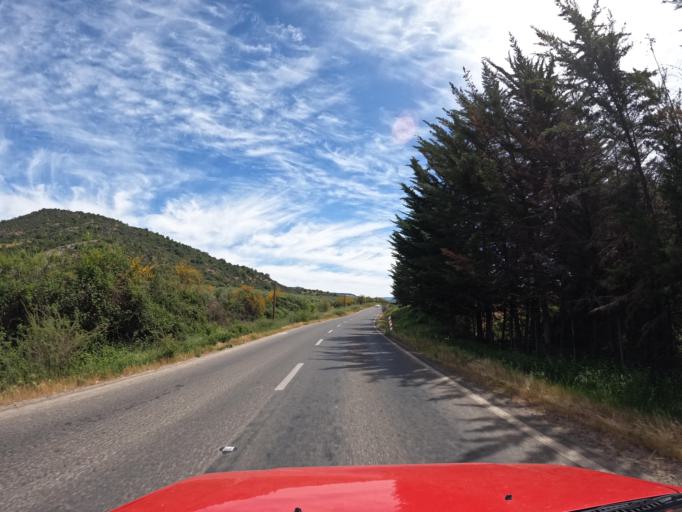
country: CL
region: Maule
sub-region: Provincia de Talca
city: Talca
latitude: -35.1213
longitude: -71.6520
